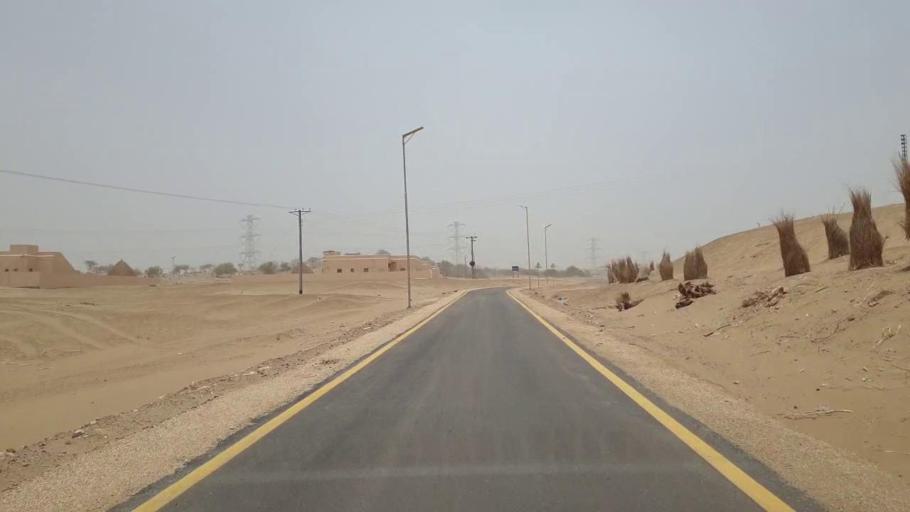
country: PK
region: Sindh
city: Islamkot
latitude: 24.7230
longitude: 70.3261
